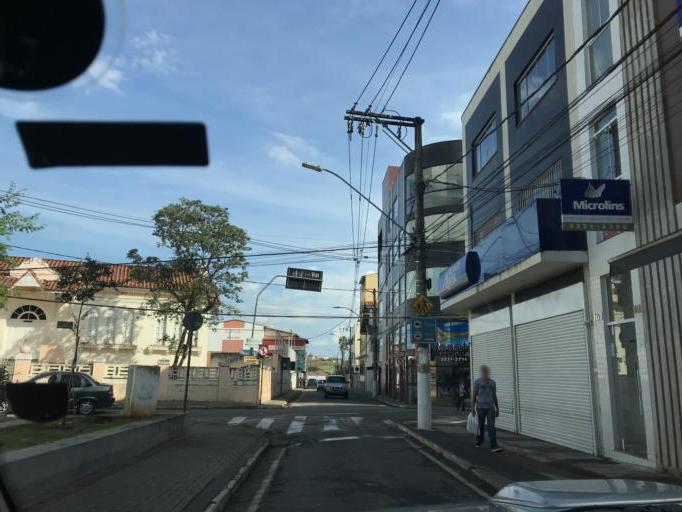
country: BR
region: Minas Gerais
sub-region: Tres Coracoes
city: Tres Coracoes
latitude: -21.6998
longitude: -45.2564
